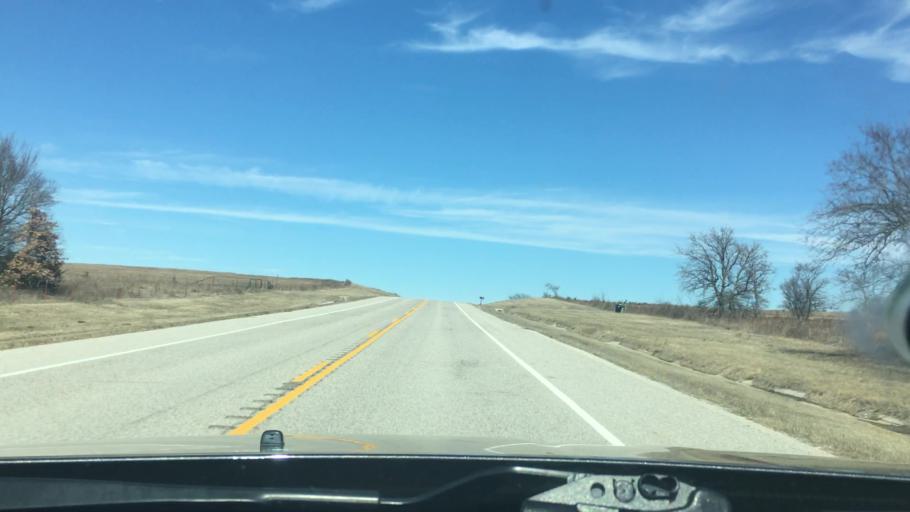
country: US
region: Oklahoma
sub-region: Carter County
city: Dickson
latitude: 34.3388
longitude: -96.9509
